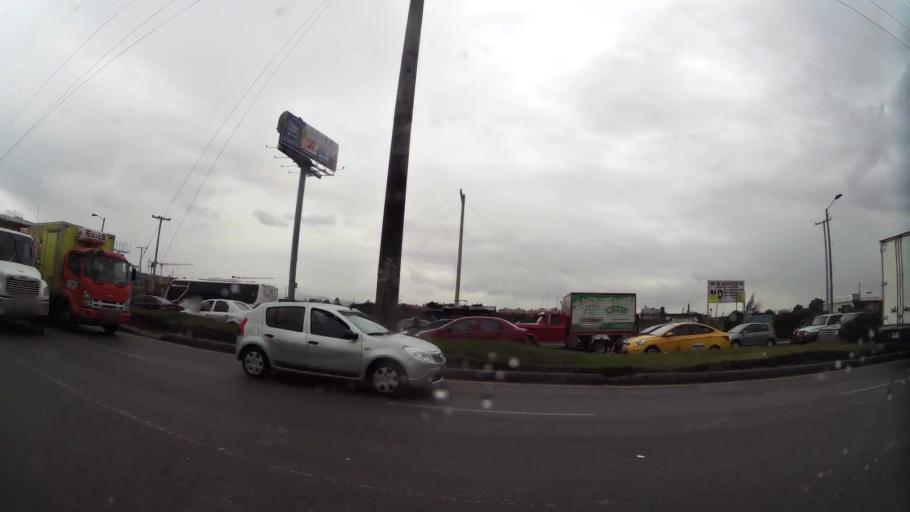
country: CO
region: Bogota D.C.
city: Bogota
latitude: 4.6511
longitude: -74.1281
